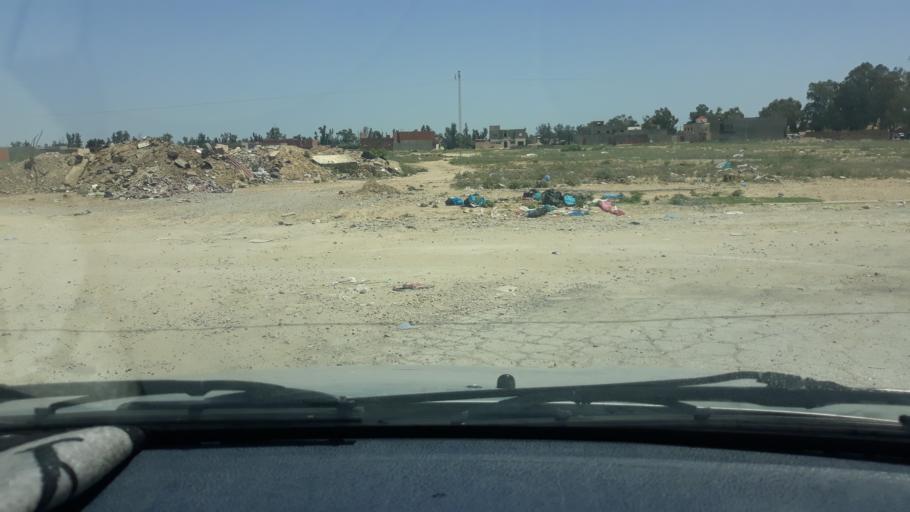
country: TN
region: Al Qayrawan
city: Kairouan
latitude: 35.6183
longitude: 9.9300
